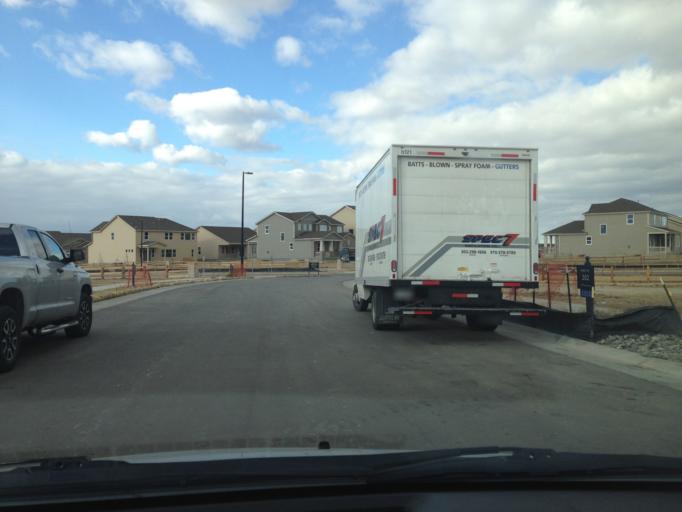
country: US
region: Colorado
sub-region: Boulder County
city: Lafayette
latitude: 40.0249
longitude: -105.0850
